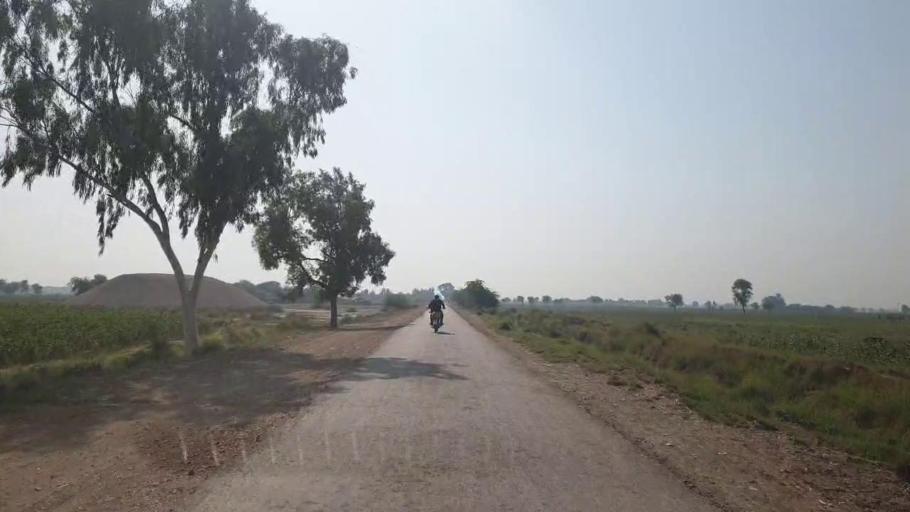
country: PK
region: Sindh
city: Shahdadpur
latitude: 25.9316
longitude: 68.7308
